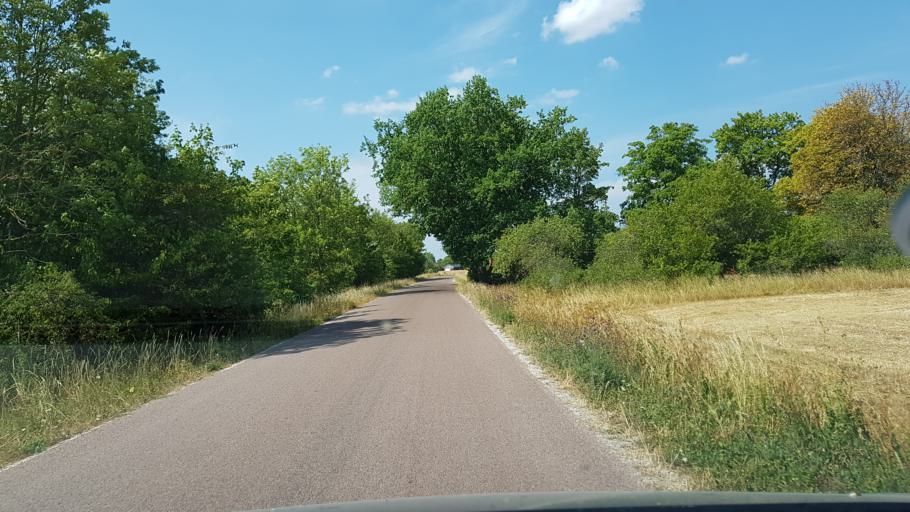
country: SE
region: Gotland
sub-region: Gotland
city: Visby
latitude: 57.6651
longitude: 18.3729
